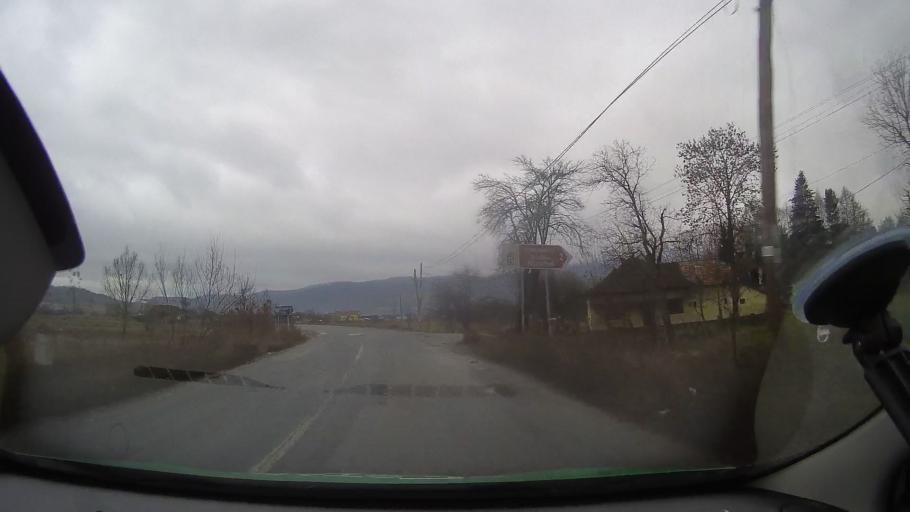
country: RO
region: Arad
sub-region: Comuna Halmagiu
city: Halmagiu
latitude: 46.2588
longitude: 22.5765
